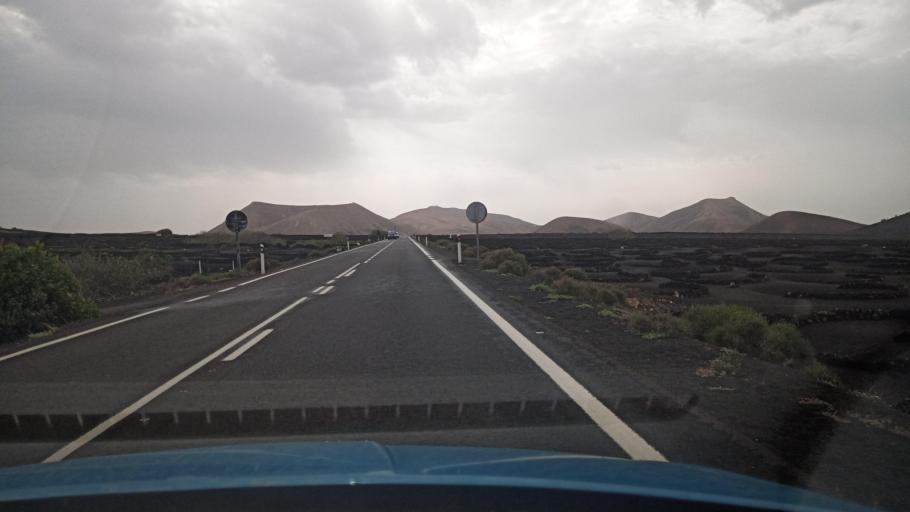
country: ES
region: Canary Islands
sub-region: Provincia de Las Palmas
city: Yaiza
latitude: 28.9590
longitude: -13.7311
